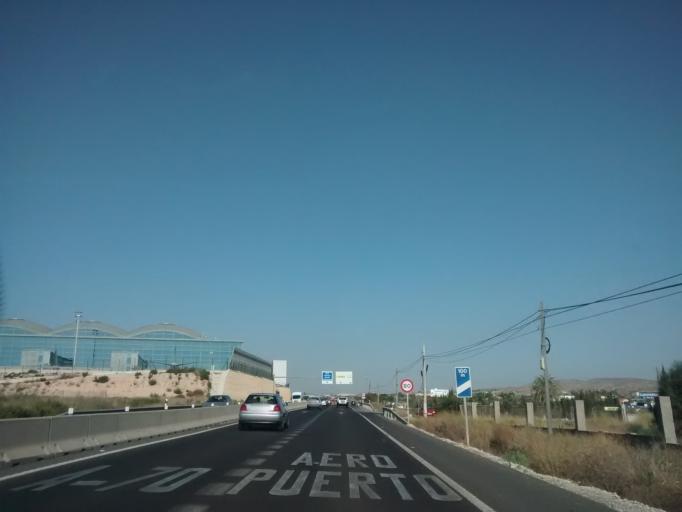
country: ES
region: Valencia
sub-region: Provincia de Alicante
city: Alicante
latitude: 38.2877
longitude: -0.5470
